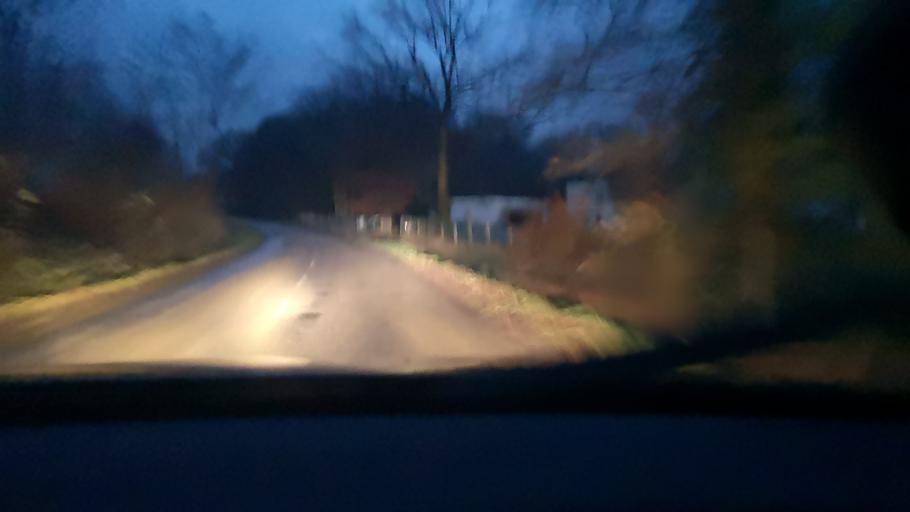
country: FR
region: Bourgogne
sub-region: Departement de Saone-et-Loire
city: Champforgeuil
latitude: 46.8476
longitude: 4.8389
